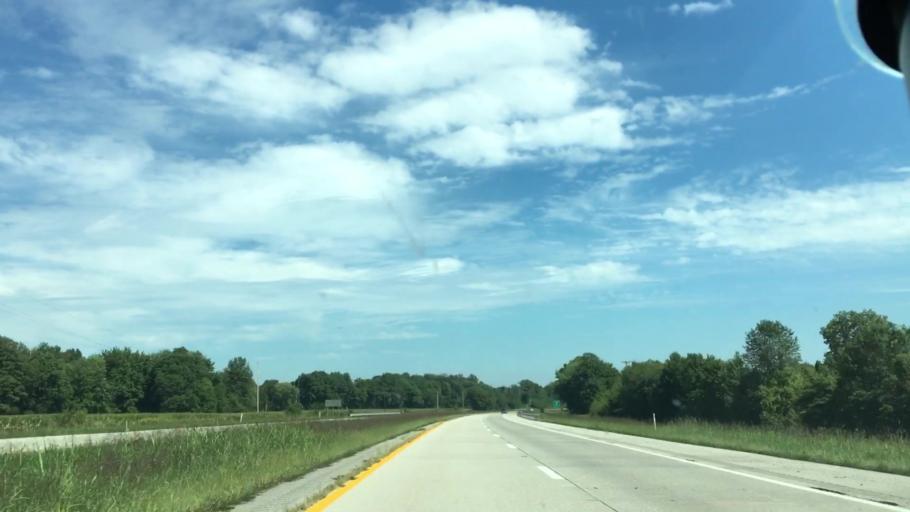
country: US
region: Kentucky
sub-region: Daviess County
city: Owensboro
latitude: 37.7674
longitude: -87.2099
